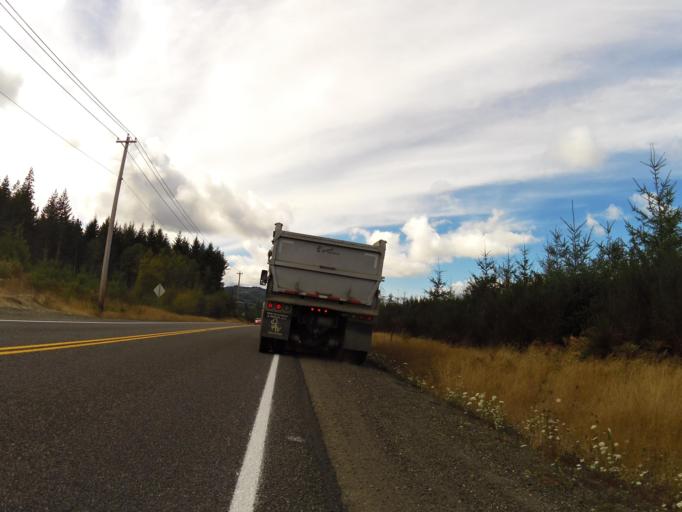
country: US
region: Washington
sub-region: Mason County
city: Shelton
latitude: 47.1478
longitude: -123.0726
